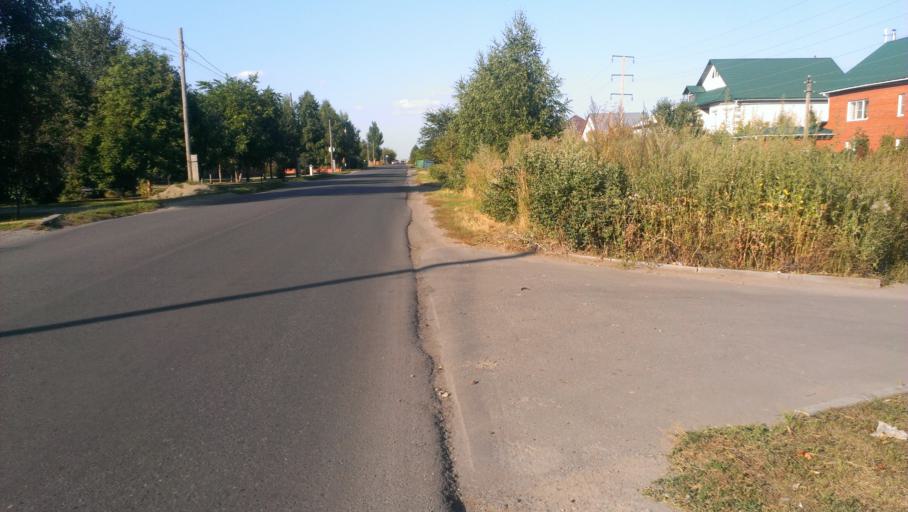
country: RU
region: Altai Krai
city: Novosilikatnyy
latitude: 53.3601
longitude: 83.6406
